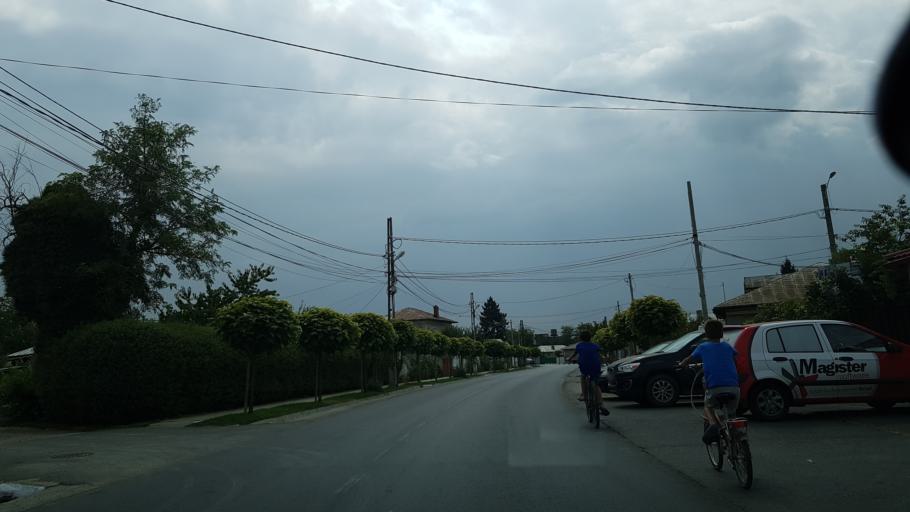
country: RO
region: Ilfov
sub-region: Comuna Branesti
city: Branesti
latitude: 44.4590
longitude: 26.3342
